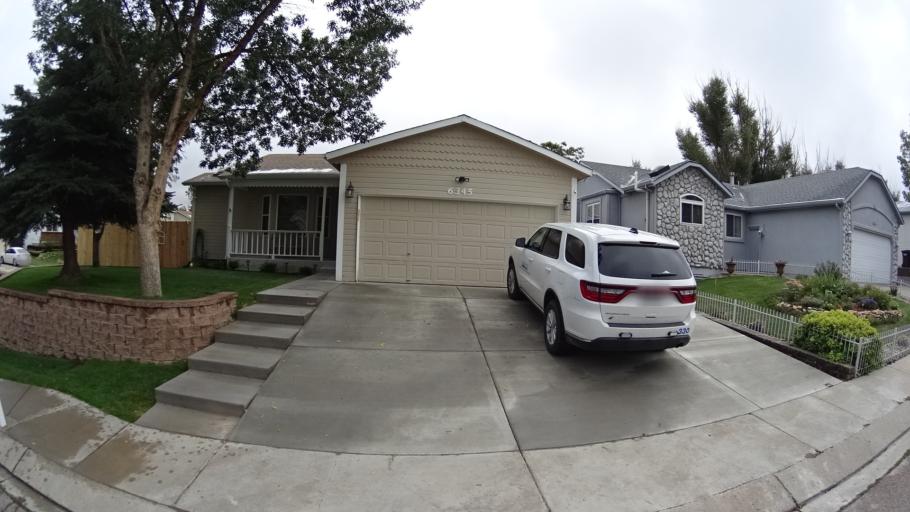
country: US
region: Colorado
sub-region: El Paso County
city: Cimarron Hills
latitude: 38.9231
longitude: -104.7644
